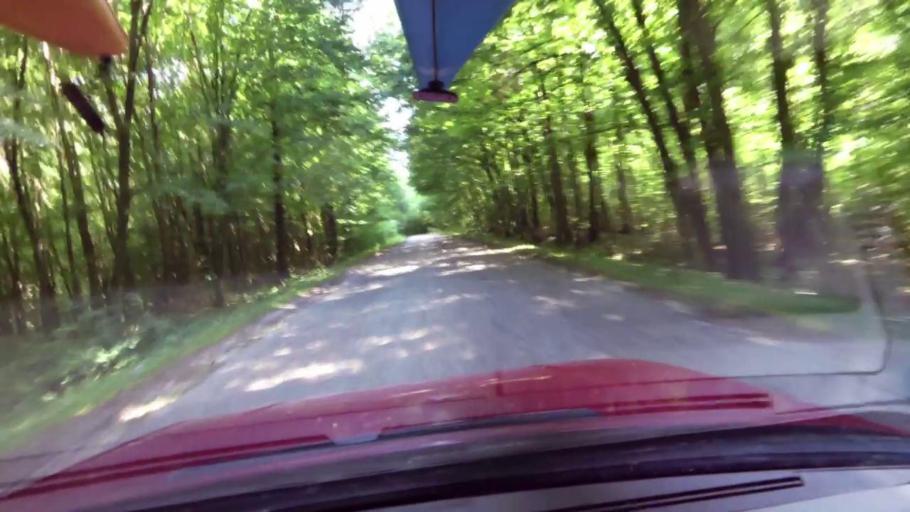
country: PL
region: Pomeranian Voivodeship
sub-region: Powiat slupski
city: Kepice
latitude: 54.1612
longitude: 16.9073
